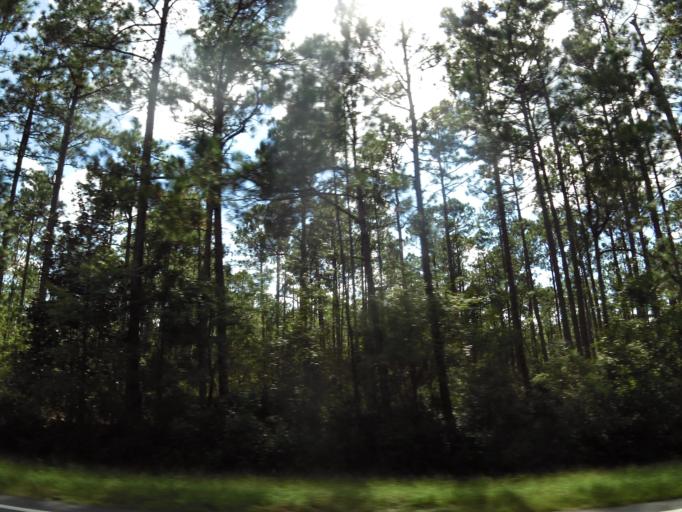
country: US
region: Georgia
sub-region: Echols County
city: Statenville
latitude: 30.7267
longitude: -83.0797
